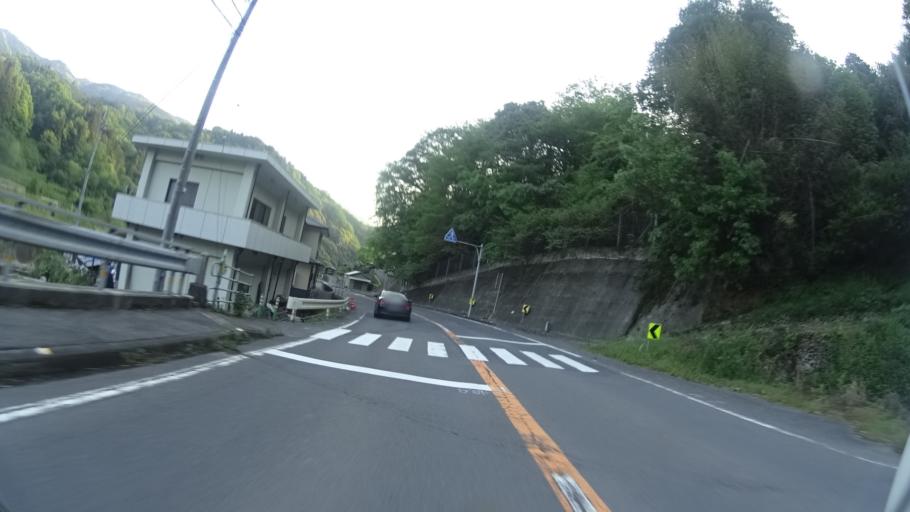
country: JP
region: Ehime
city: Kawanoecho
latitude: 33.9963
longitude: 133.6528
